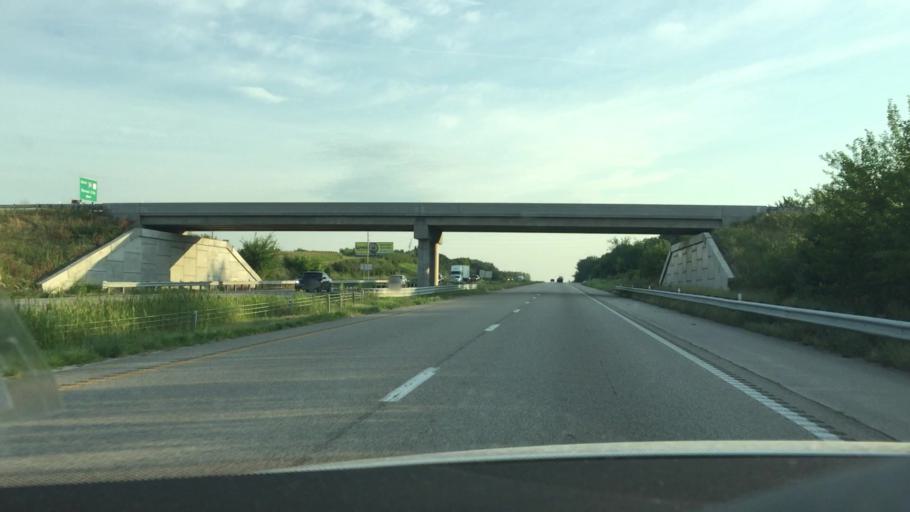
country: US
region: Missouri
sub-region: Platte County
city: Platte City
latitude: 39.4504
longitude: -94.7886
